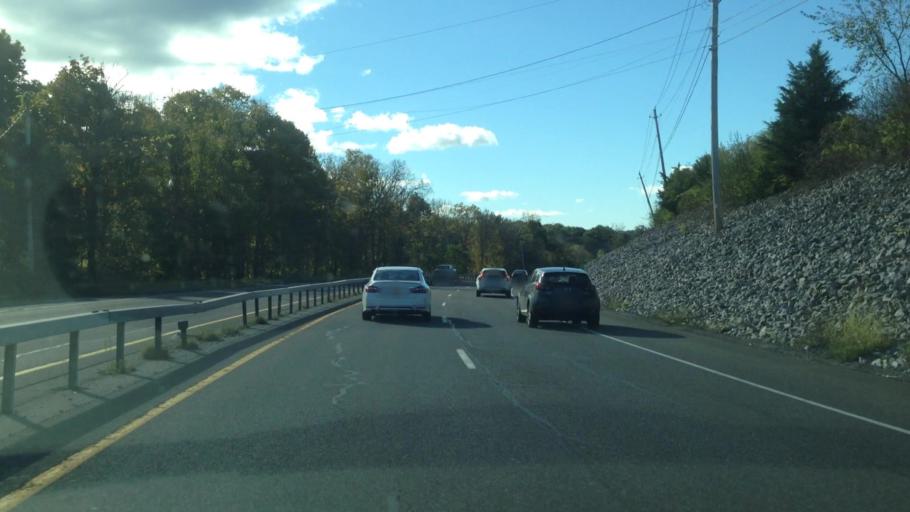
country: US
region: New York
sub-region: Ulster County
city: Highland
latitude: 41.7356
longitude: -73.9613
